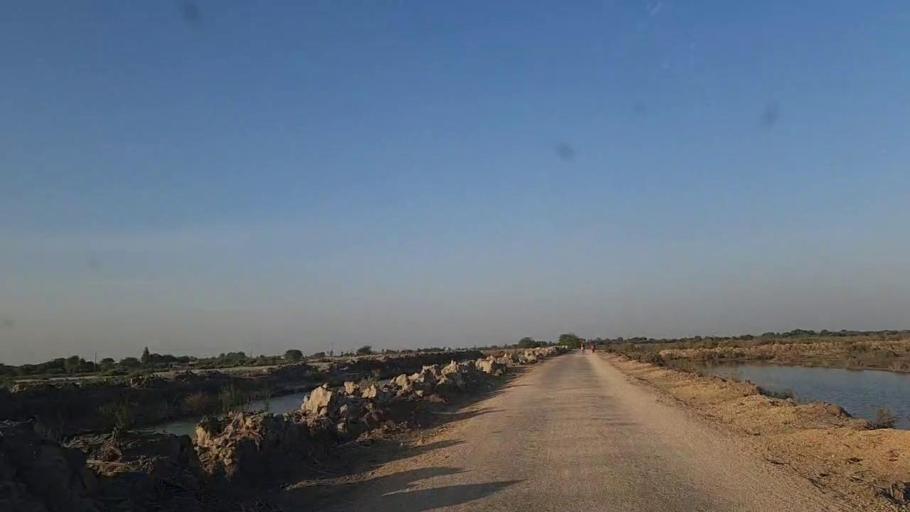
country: PK
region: Sindh
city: Mirpur Batoro
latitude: 24.6943
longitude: 68.2002
